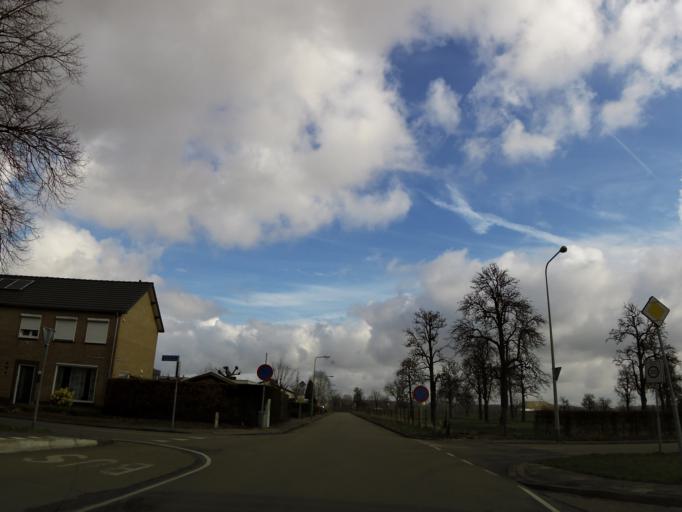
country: NL
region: Limburg
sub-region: Gemeente Maastricht
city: Maastricht
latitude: 50.8791
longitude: 5.6875
